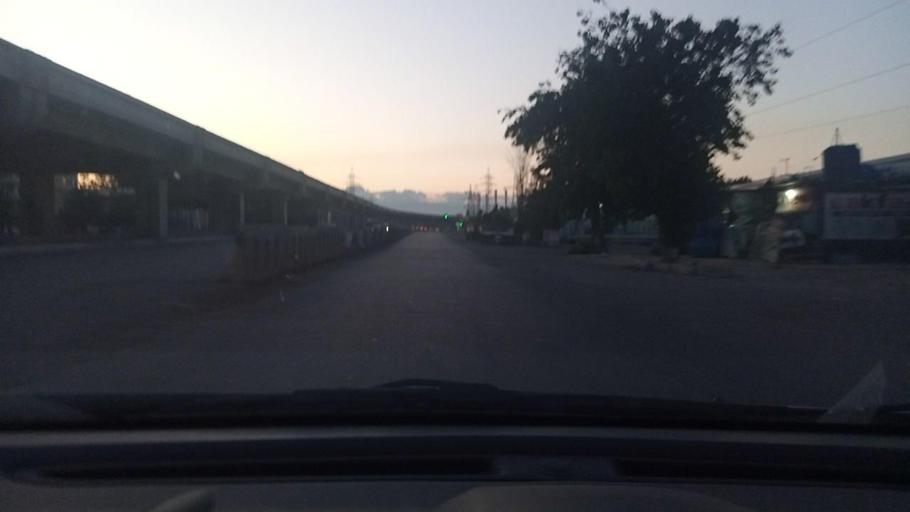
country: UZ
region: Toshkent Shahri
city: Bektemir
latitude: 41.2442
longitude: 69.3072
